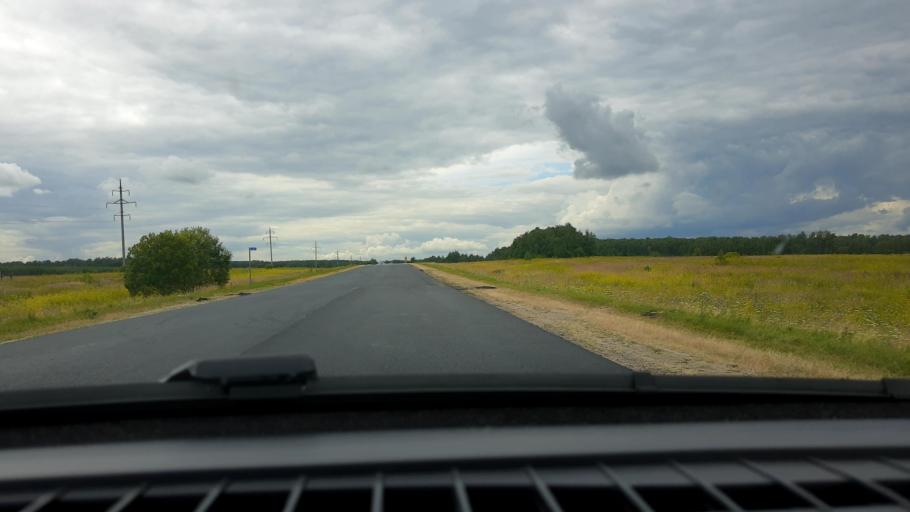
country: RU
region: Nizjnij Novgorod
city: Bol'shoye Murashkino
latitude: 55.8023
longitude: 44.8780
